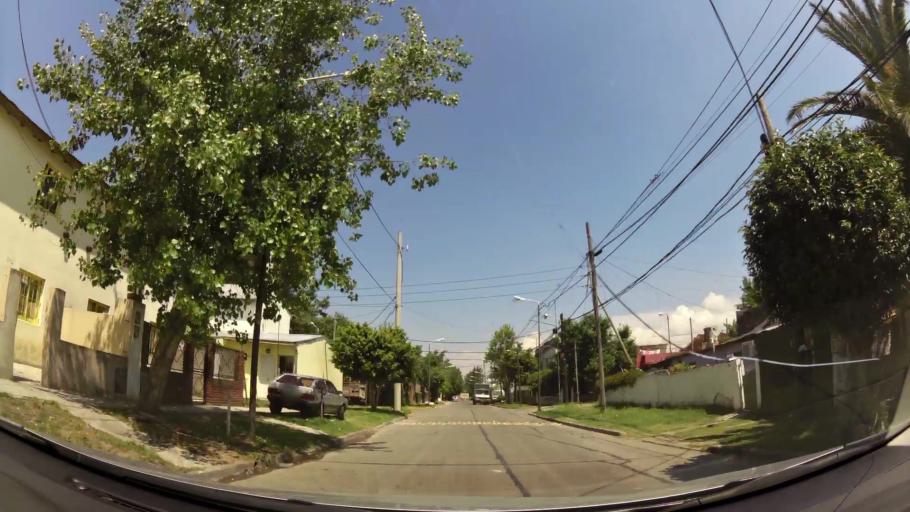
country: AR
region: Buenos Aires
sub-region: Partido de Tigre
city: Tigre
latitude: -34.4591
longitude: -58.5826
